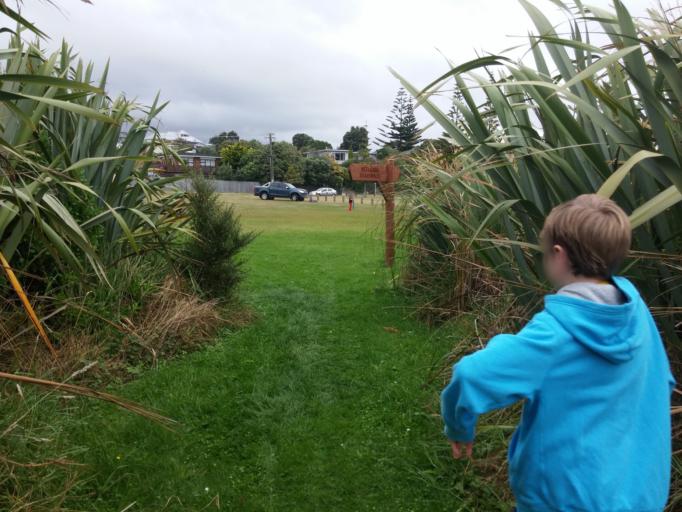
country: NZ
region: Wellington
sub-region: Kapiti Coast District
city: Paraparaumu
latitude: -40.8691
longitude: 175.0197
